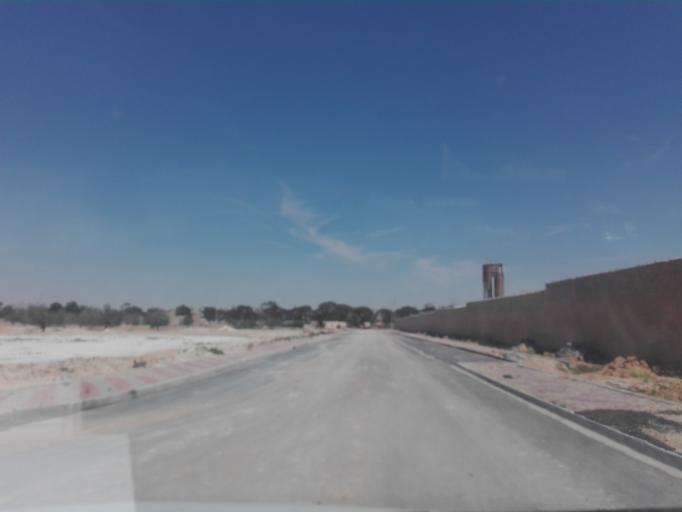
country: TN
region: Safaqis
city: Sfax
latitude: 34.7271
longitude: 10.5195
